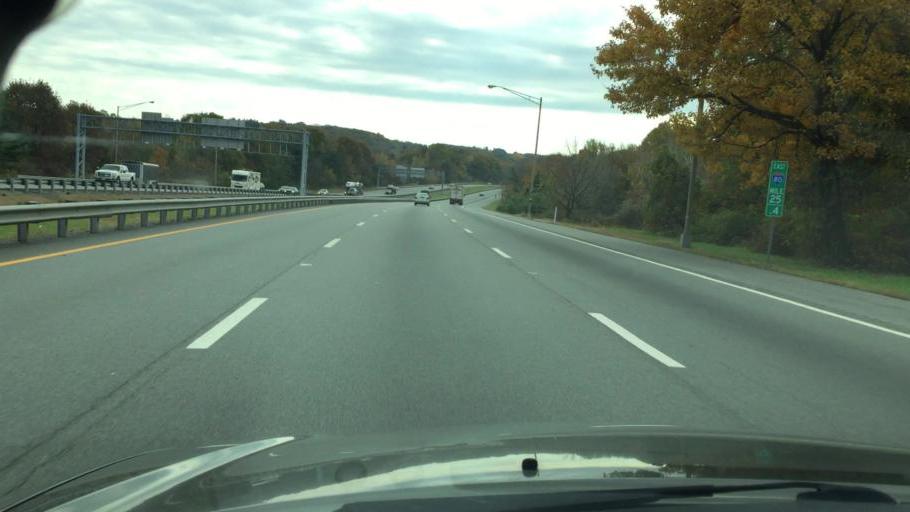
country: US
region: New Jersey
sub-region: Sussex County
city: Stanhope
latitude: 40.9041
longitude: -74.7226
